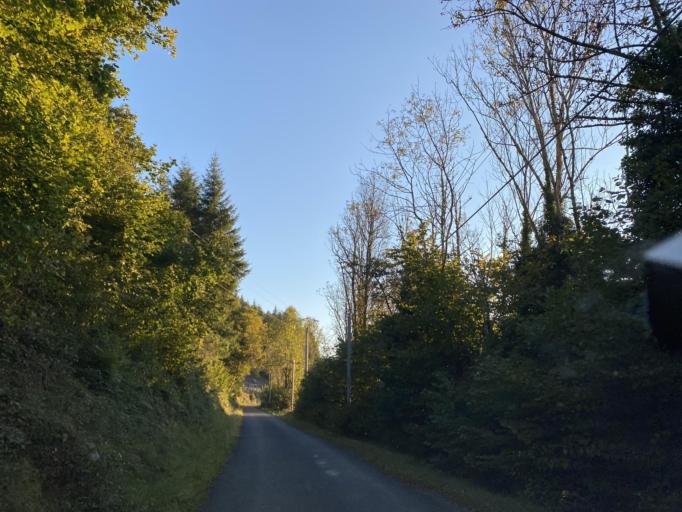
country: FR
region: Rhone-Alpes
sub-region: Departement de la Loire
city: Saint-Just-en-Chevalet
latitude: 45.9268
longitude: 3.8472
